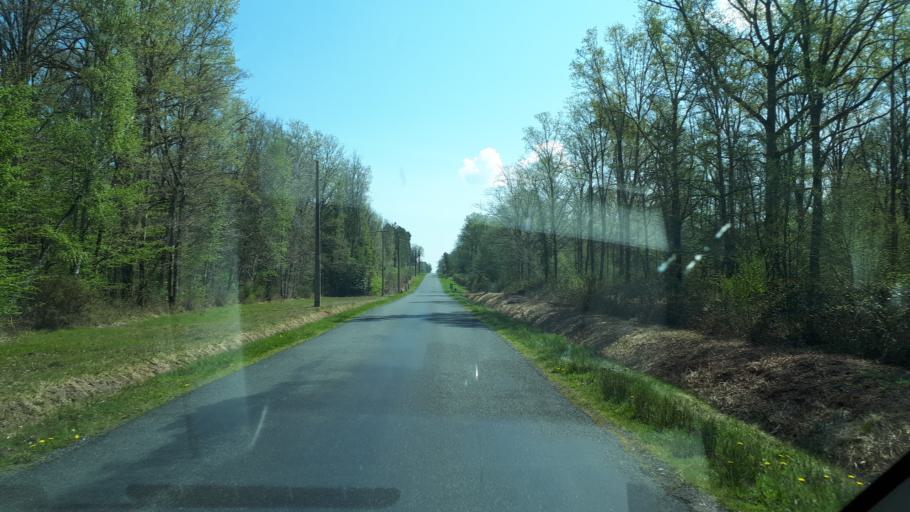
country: FR
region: Centre
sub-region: Departement du Cher
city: Neuvy-sur-Barangeon
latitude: 47.3195
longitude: 2.2029
